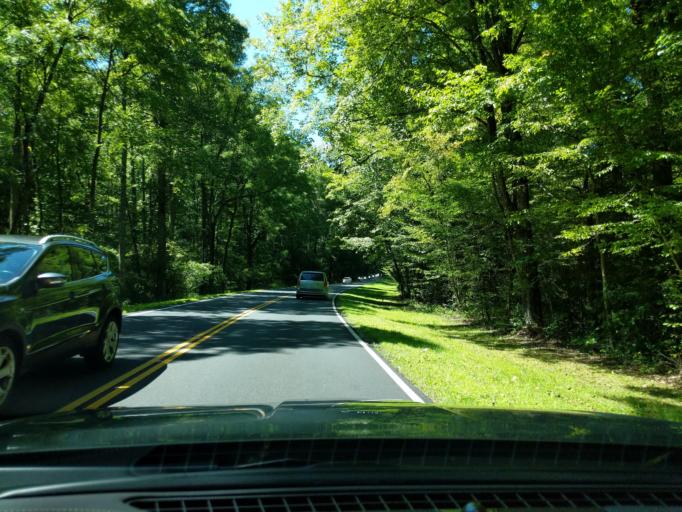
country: US
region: North Carolina
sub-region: Swain County
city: Cherokee
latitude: 35.5575
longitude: -83.3207
